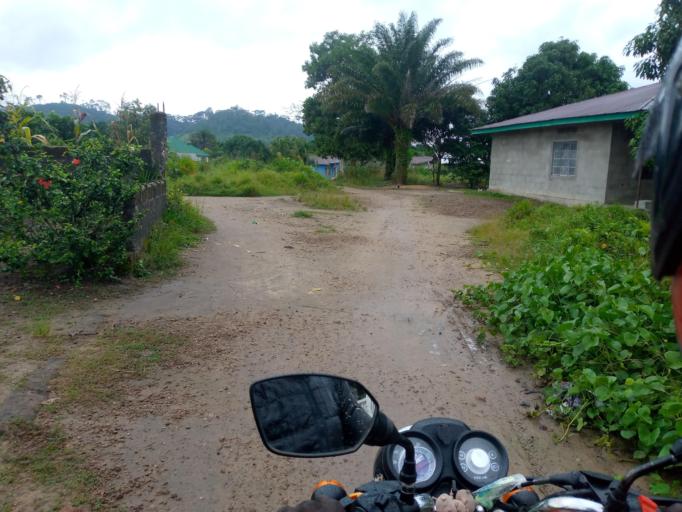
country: SL
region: Eastern Province
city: Kenema
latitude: 7.8437
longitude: -11.2063
